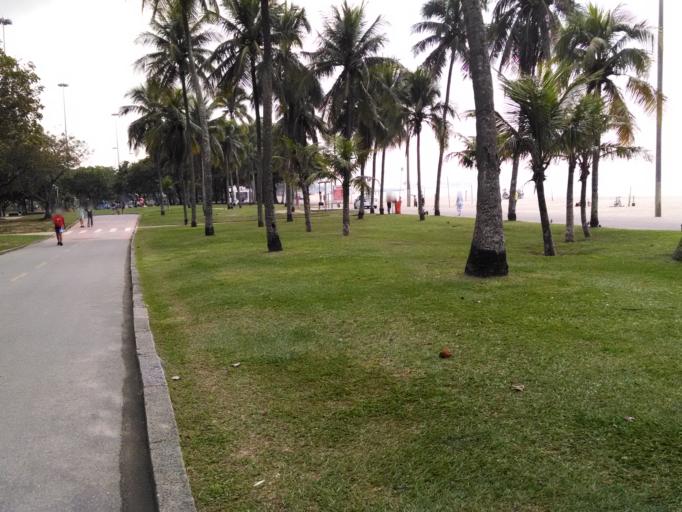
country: BR
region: Rio de Janeiro
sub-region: Rio De Janeiro
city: Rio de Janeiro
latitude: -22.9315
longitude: -43.1723
